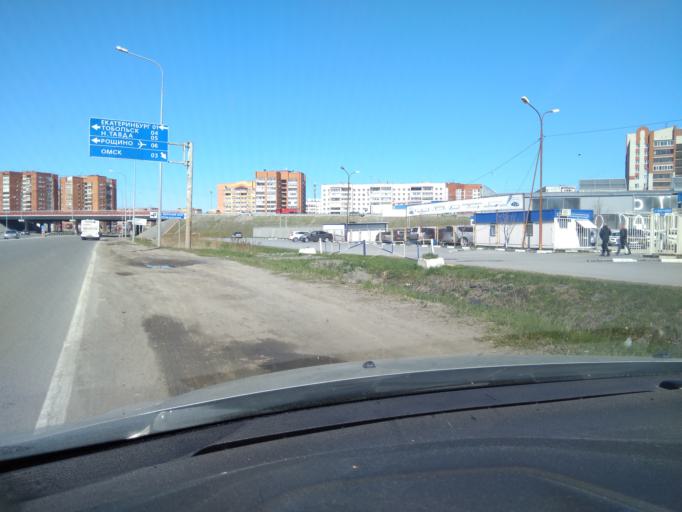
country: RU
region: Tjumen
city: Tyumen
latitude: 57.1181
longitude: 65.5213
